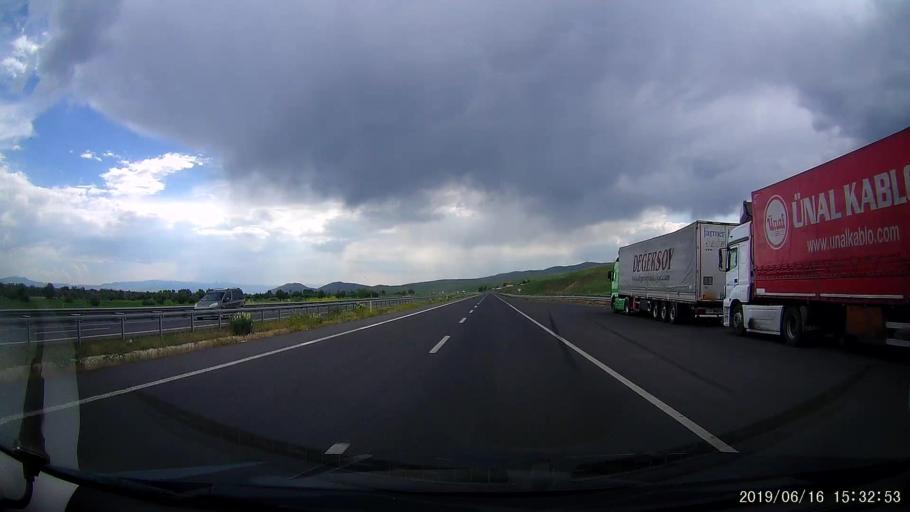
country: TR
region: Erzurum
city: Horasan
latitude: 40.0296
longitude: 42.0352
